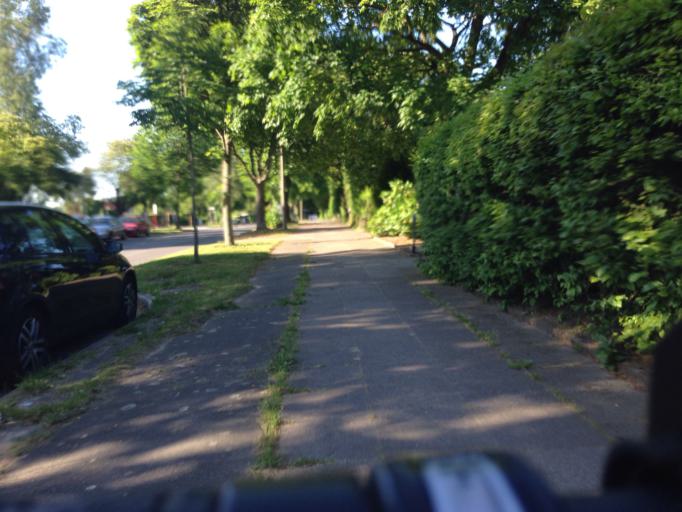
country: DE
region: Schleswig-Holstein
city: Barsbuettel
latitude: 53.5904
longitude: 10.1849
